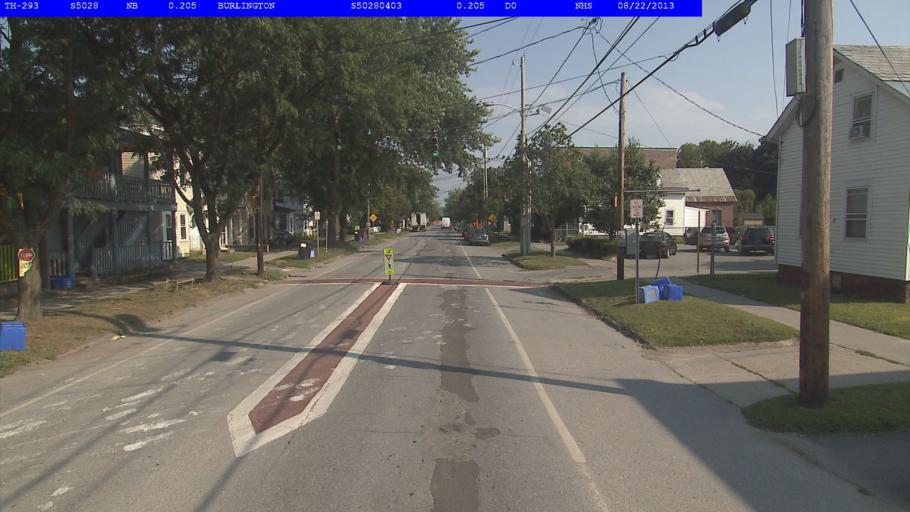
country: US
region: Vermont
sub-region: Chittenden County
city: Burlington
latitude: 44.4833
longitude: -73.2176
